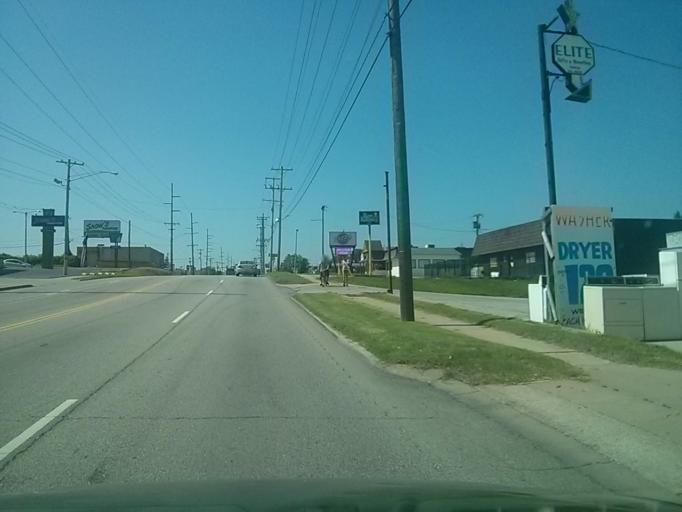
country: US
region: Oklahoma
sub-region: Tulsa County
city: Tulsa
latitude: 36.1505
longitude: -95.9046
